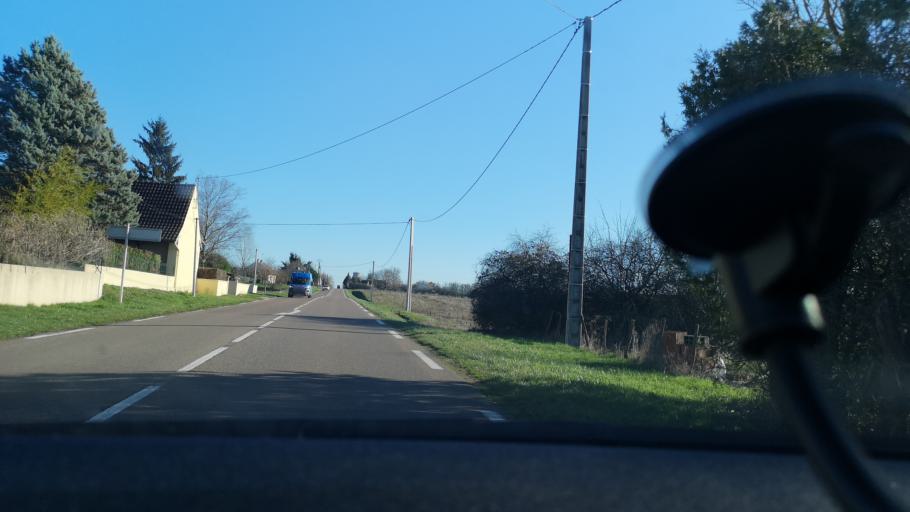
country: FR
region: Bourgogne
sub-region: Departement de Saone-et-Loire
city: Ouroux-sur-Saone
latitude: 46.7589
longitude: 4.9970
